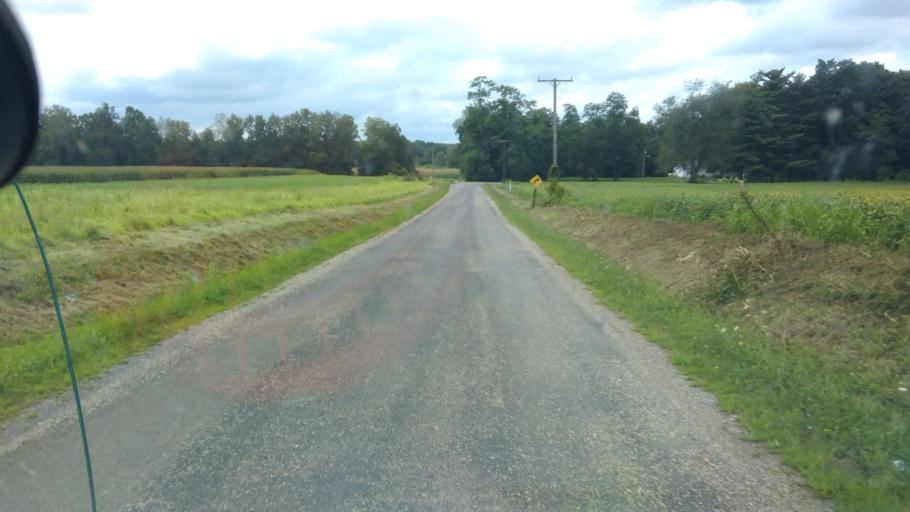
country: US
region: Ohio
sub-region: Richland County
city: Lincoln Heights
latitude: 40.8210
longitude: -82.4051
